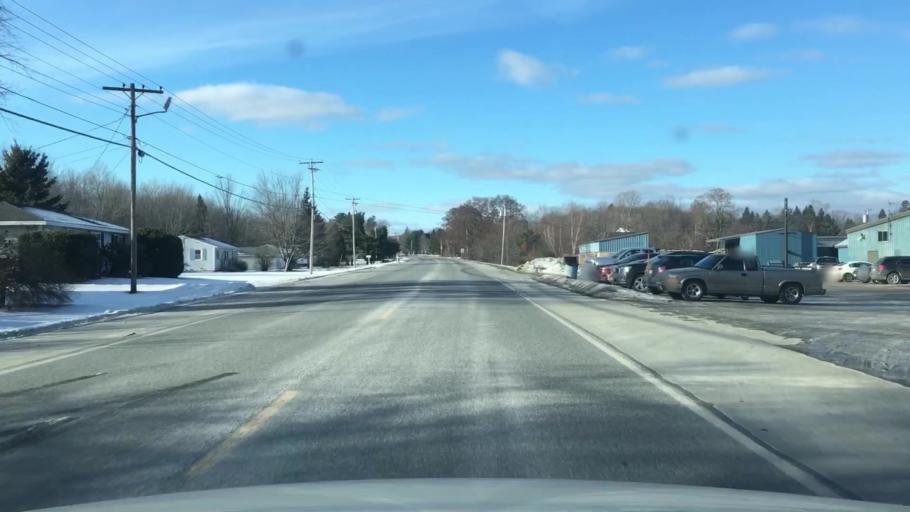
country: US
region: Maine
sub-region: Penobscot County
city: Eddington
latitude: 44.8245
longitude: -68.6532
